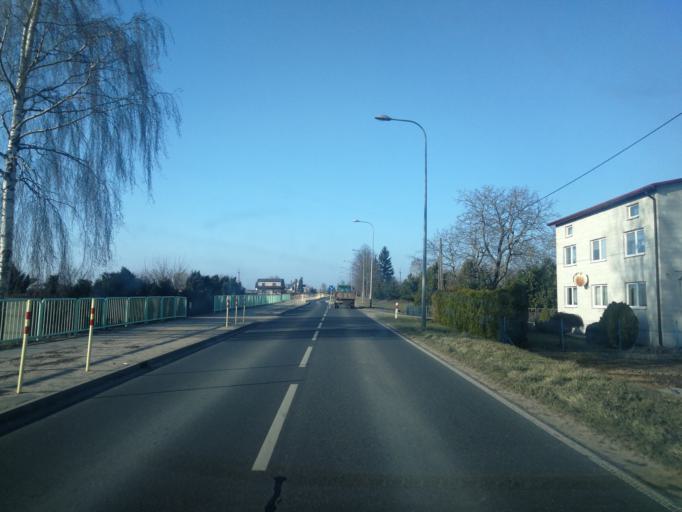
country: PL
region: Warmian-Masurian Voivodeship
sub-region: Powiat ilawski
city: Lubawa
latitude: 53.4678
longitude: 19.7711
